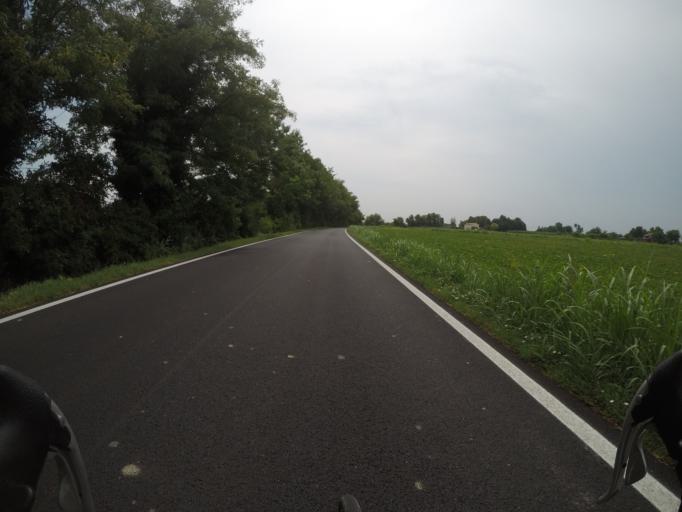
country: IT
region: Veneto
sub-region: Provincia di Rovigo
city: Costa di Rovigo
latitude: 45.0519
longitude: 11.6718
